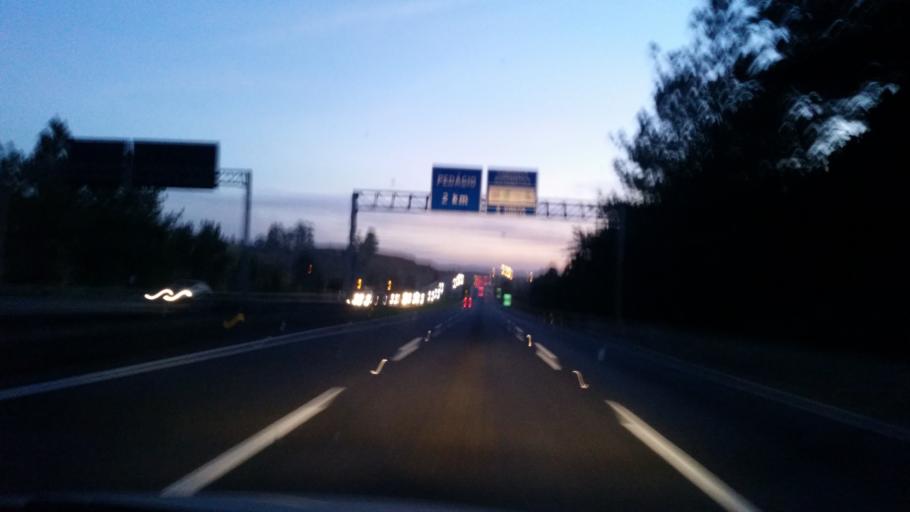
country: BR
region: Sao Paulo
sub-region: Santa Isabel
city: Santa Isabel
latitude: -23.3722
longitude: -46.1382
